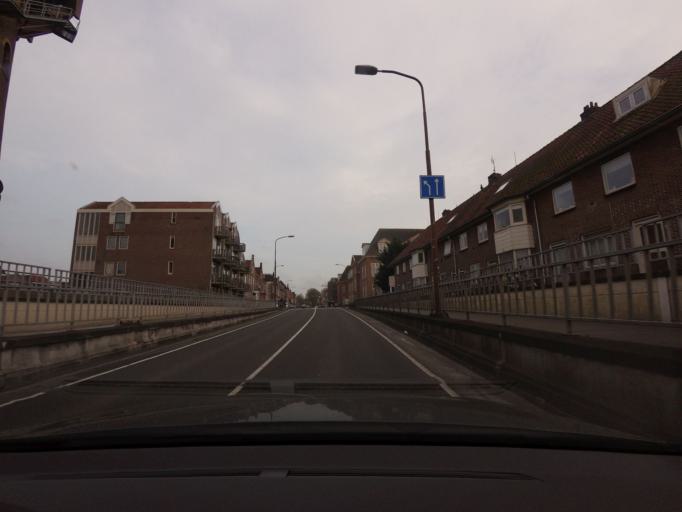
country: NL
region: North Holland
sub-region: Gemeente Alkmaar
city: Alkmaar
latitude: 52.6364
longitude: 4.7363
